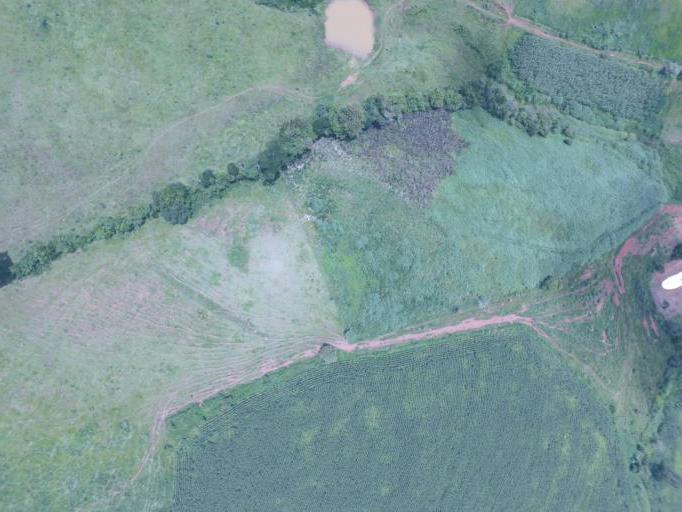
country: BR
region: Minas Gerais
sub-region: Tiradentes
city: Tiradentes
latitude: -21.0911
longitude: -44.0764
